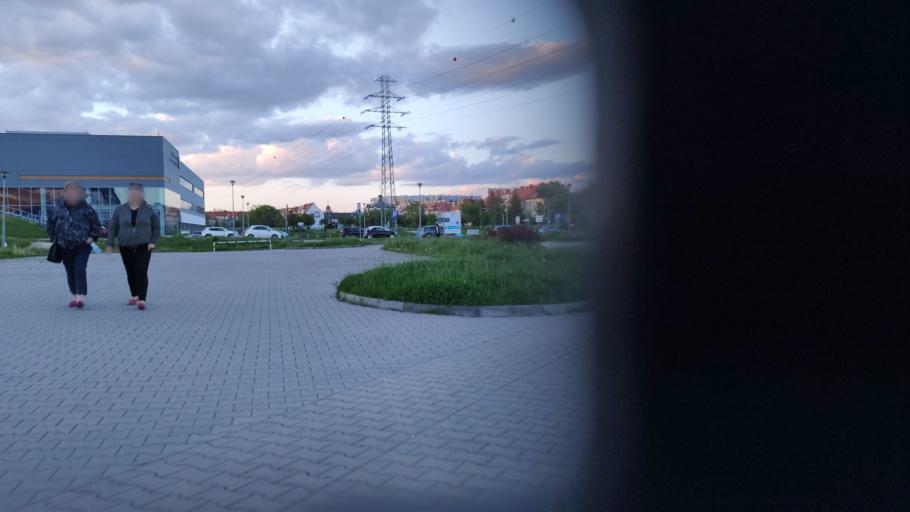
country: PL
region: Lower Silesian Voivodeship
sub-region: Powiat wroclawski
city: Wroclaw
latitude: 51.0750
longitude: 17.0317
